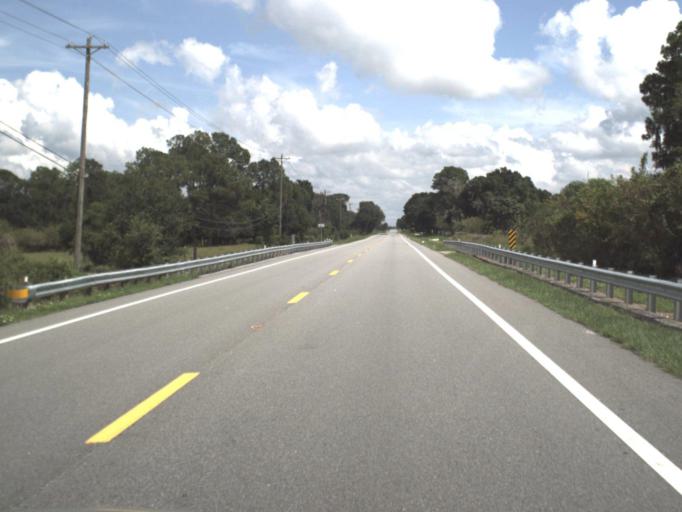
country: US
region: Florida
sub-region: Hardee County
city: Wauchula
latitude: 27.4600
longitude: -82.1116
